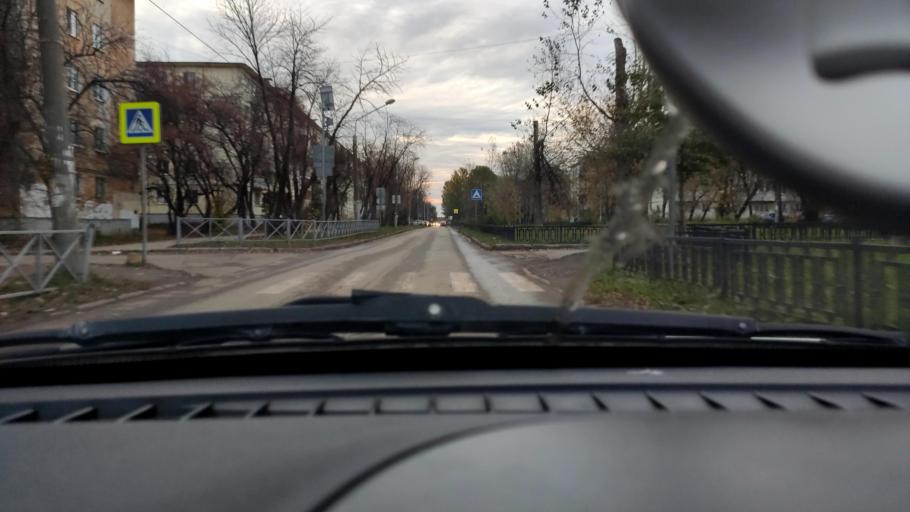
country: RU
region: Perm
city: Perm
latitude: 57.9965
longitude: 56.2955
